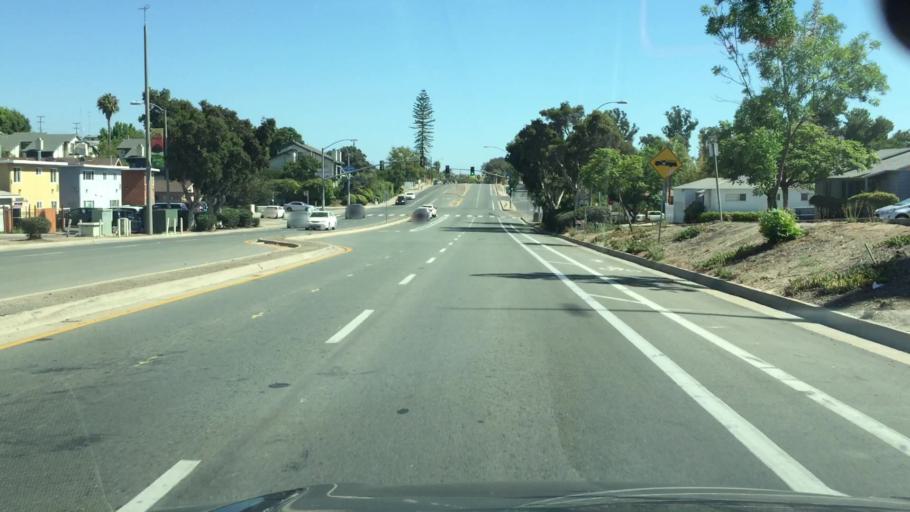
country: US
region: California
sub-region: San Diego County
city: Lemon Grove
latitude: 32.7371
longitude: -117.0797
